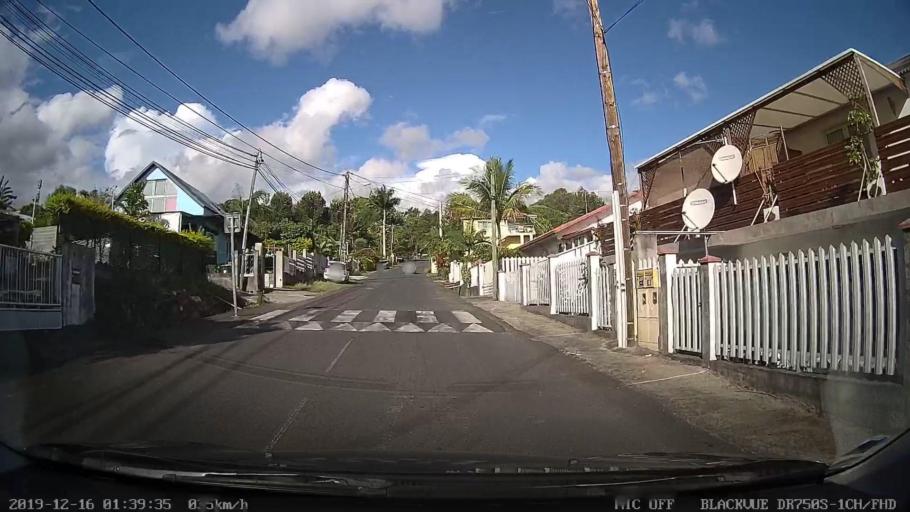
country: RE
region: Reunion
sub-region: Reunion
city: Le Tampon
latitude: -21.2619
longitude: 55.5079
